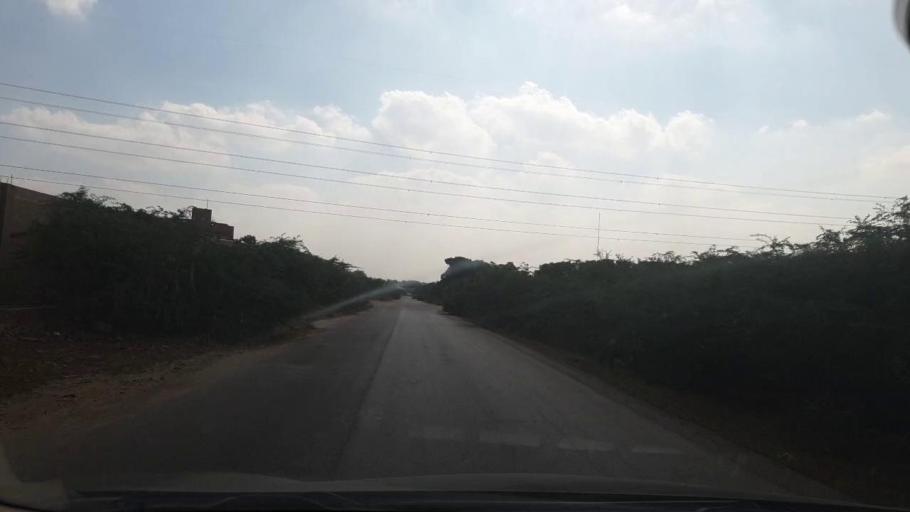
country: PK
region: Sindh
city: Malir Cantonment
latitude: 25.0105
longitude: 67.3546
